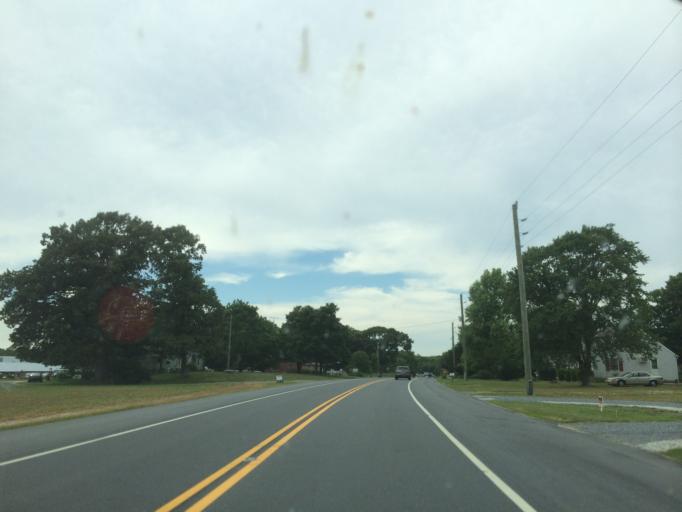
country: US
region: Delaware
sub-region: Sussex County
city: Bridgeville
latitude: 38.7900
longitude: -75.6880
